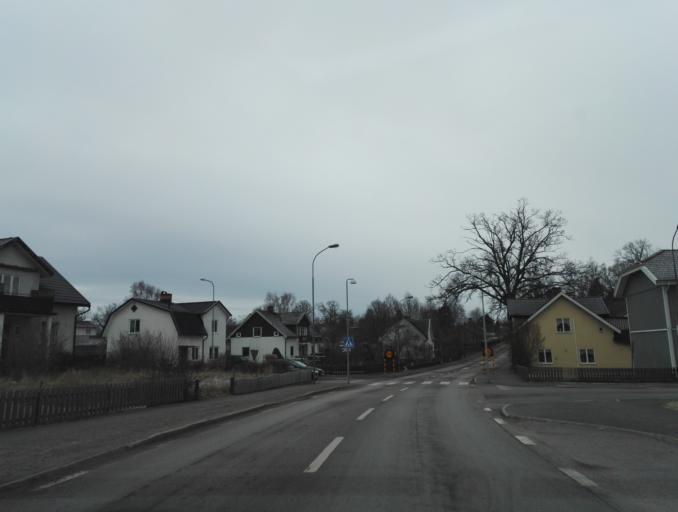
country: SE
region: Kalmar
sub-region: Hultsfreds Kommun
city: Virserum
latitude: 57.3149
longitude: 15.5851
